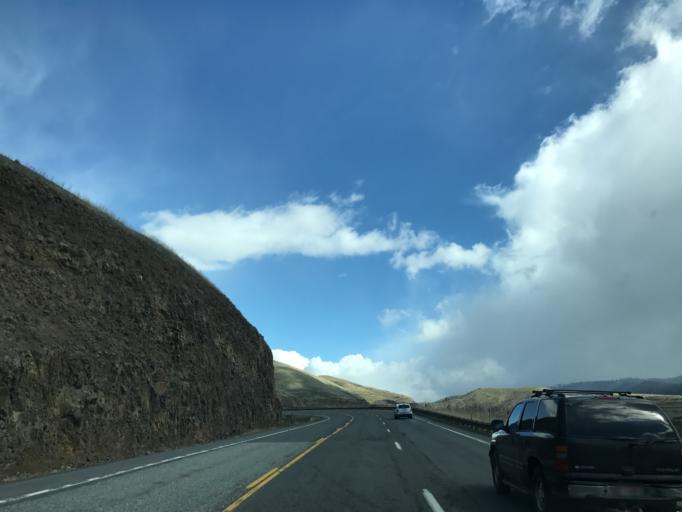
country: US
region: Idaho
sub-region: Idaho County
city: Grangeville
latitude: 45.8109
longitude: -116.2802
